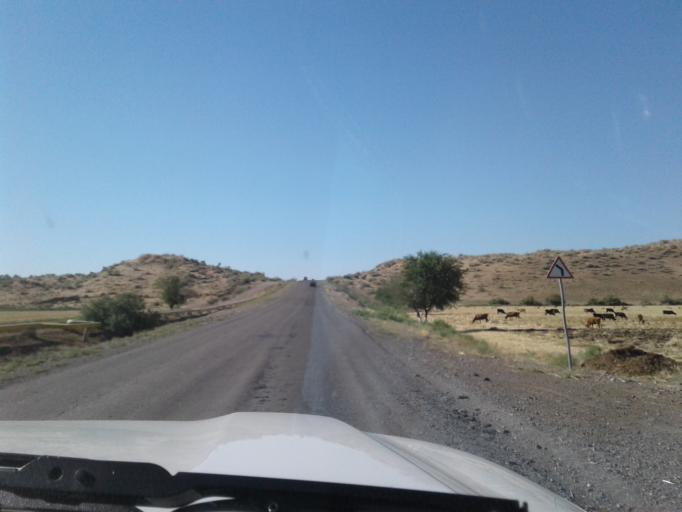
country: TM
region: Mary
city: Yoloeten
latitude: 36.6999
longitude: 62.4583
